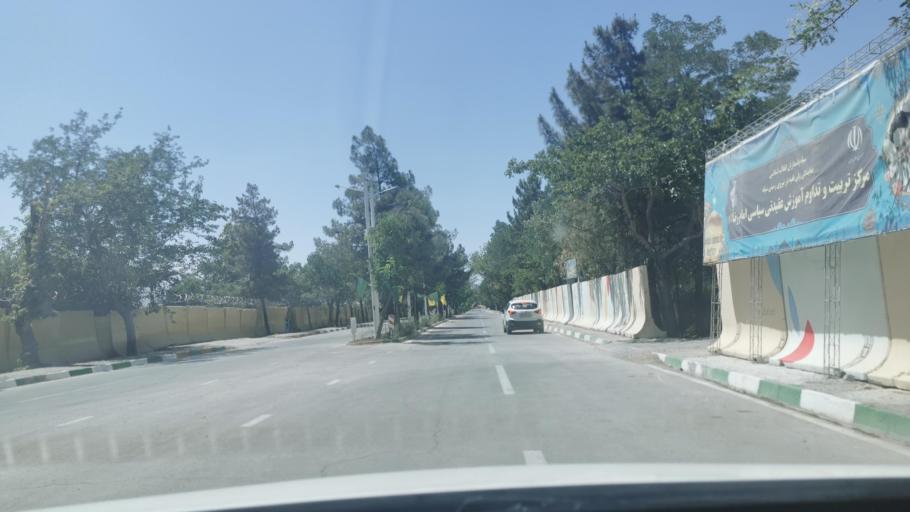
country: IR
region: Razavi Khorasan
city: Mashhad
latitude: 36.2765
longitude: 59.5860
